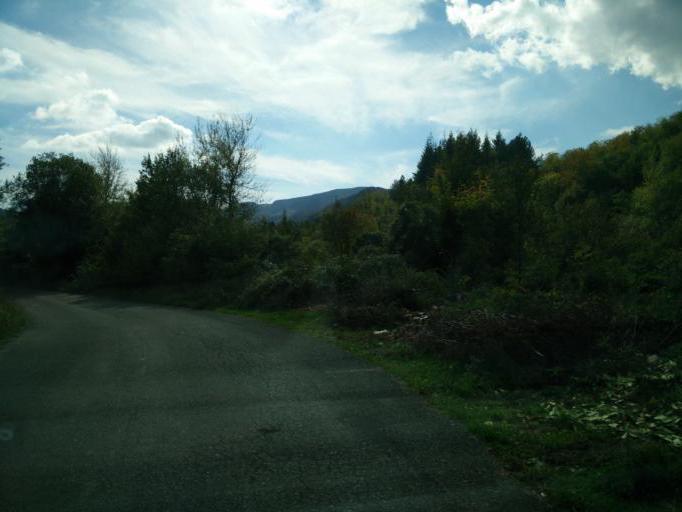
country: IT
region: Tuscany
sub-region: Provincia di Massa-Carrara
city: Patigno
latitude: 44.3590
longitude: 9.7465
